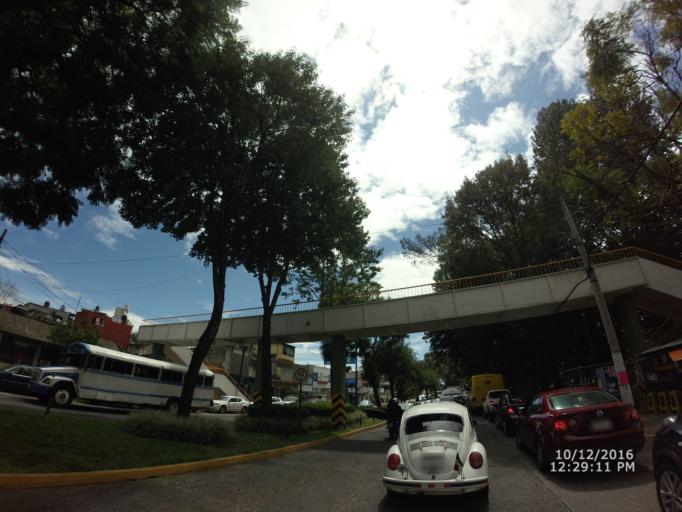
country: MX
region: Veracruz
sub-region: Xalapa
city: Xalapa de Enriquez
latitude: 19.5419
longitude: -96.9267
